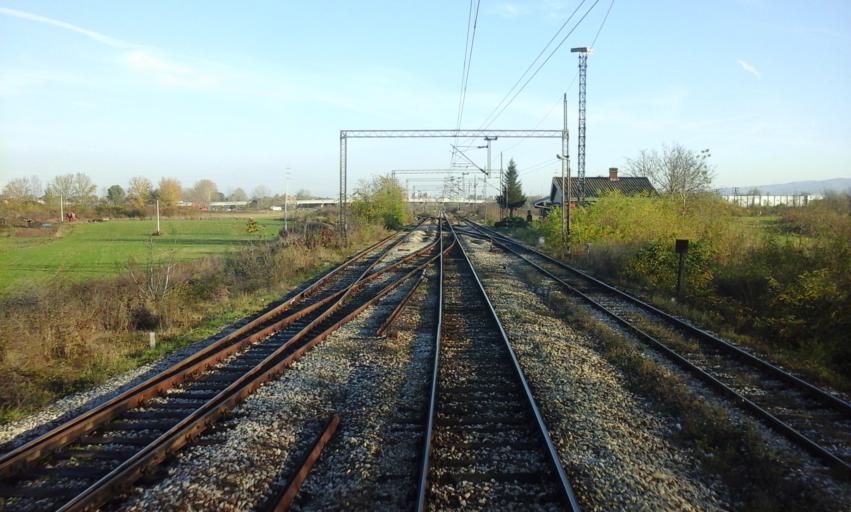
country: RS
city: Veternik
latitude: 45.2833
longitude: 19.7924
